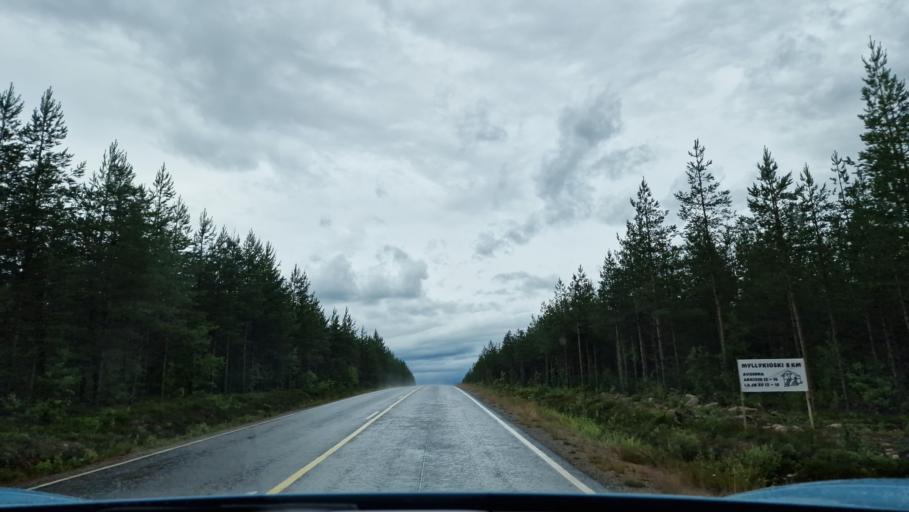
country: FI
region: Central Finland
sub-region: Saarijaervi-Viitasaari
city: Pylkoenmaeki
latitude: 62.6602
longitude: 24.5637
